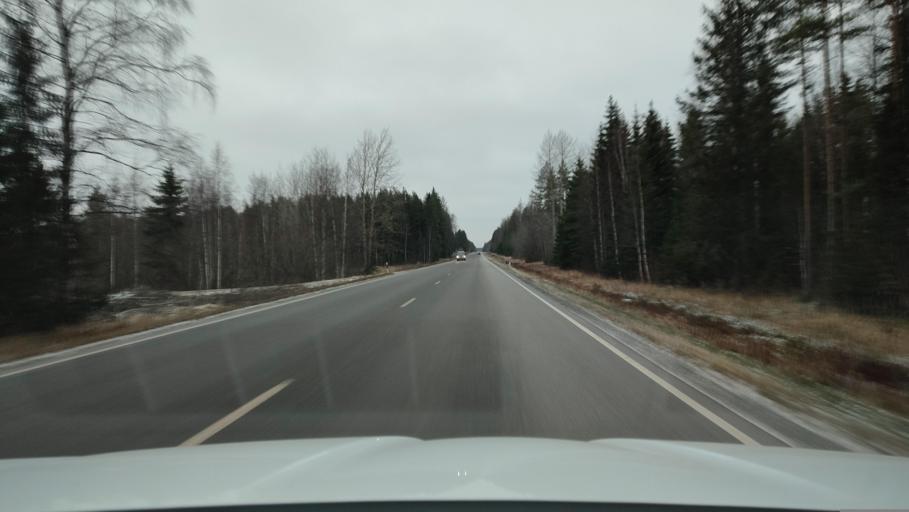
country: FI
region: Ostrobothnia
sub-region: Sydosterbotten
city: Naerpes
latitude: 62.5186
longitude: 21.4568
